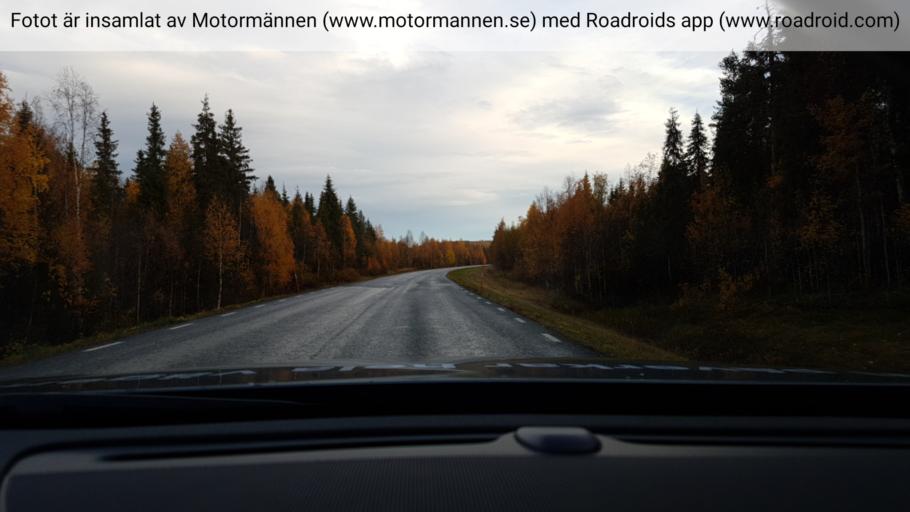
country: SE
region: Norrbotten
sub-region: Overkalix Kommun
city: OEverkalix
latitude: 66.9135
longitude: 22.7675
